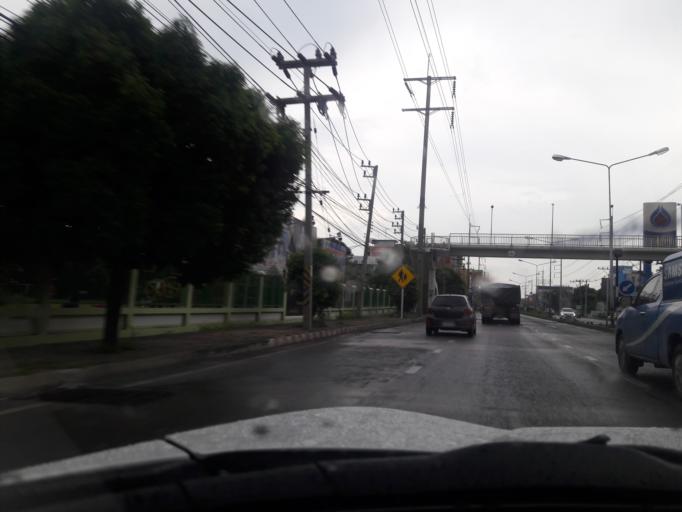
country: TH
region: Lop Buri
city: Lop Buri
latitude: 14.7947
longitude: 100.6676
